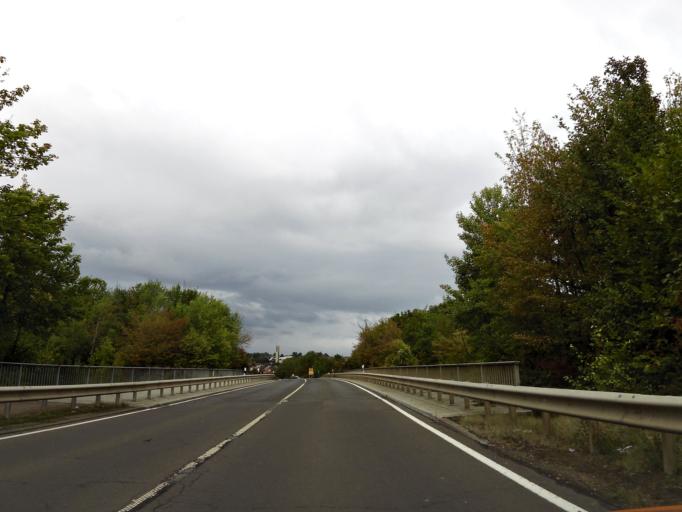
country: DE
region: Rheinland-Pfalz
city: Hackenheim
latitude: 49.8228
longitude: 7.9076
